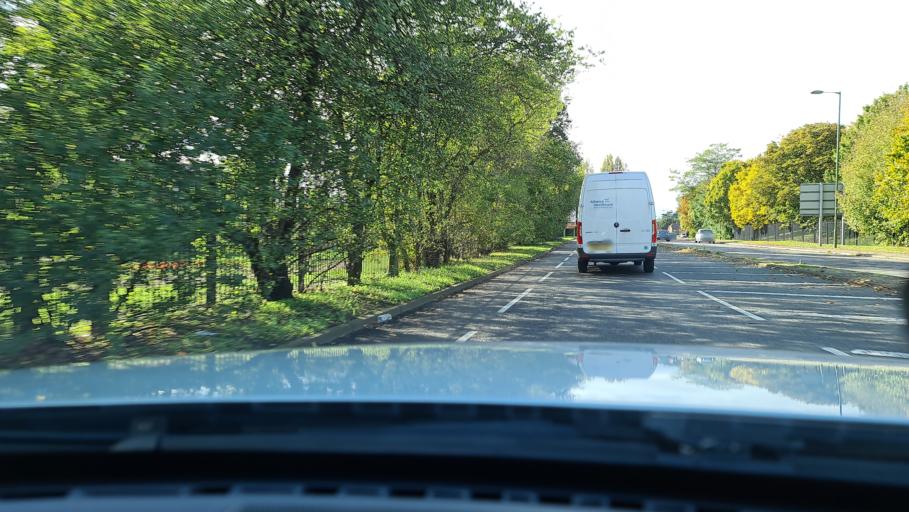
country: GB
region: England
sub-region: Surrey
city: Walton-on-Thames
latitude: 51.3686
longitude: -0.3973
